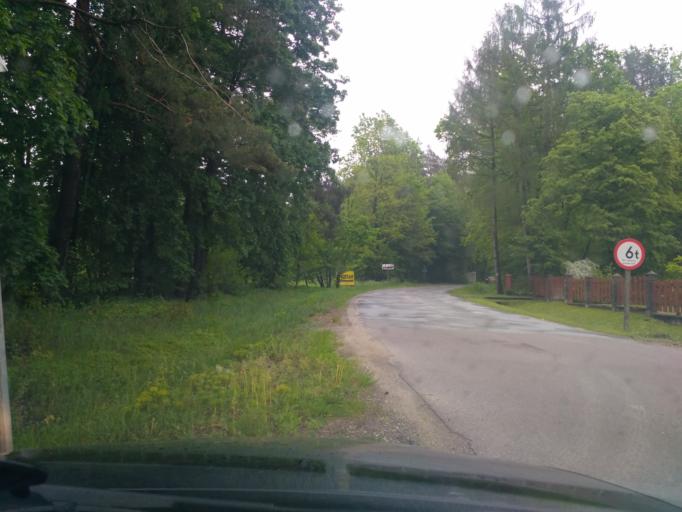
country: PL
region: Subcarpathian Voivodeship
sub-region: Powiat debicki
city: Pilzno
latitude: 49.9768
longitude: 21.3530
